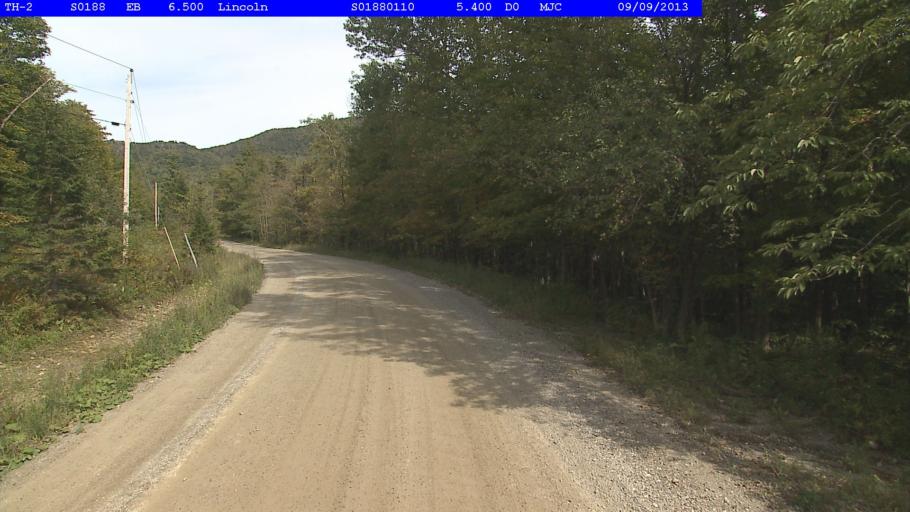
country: US
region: Vermont
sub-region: Addison County
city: Bristol
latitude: 44.0882
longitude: -72.9475
